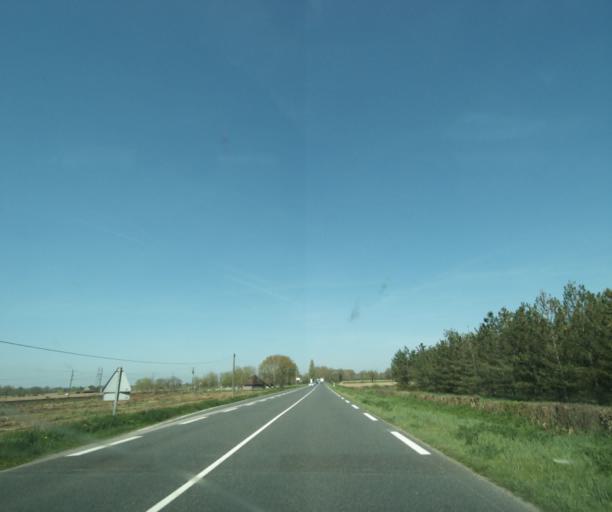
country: FR
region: Bourgogne
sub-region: Departement de la Nievre
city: Chantenay-Saint-Imbert
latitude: 46.6820
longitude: 3.2259
